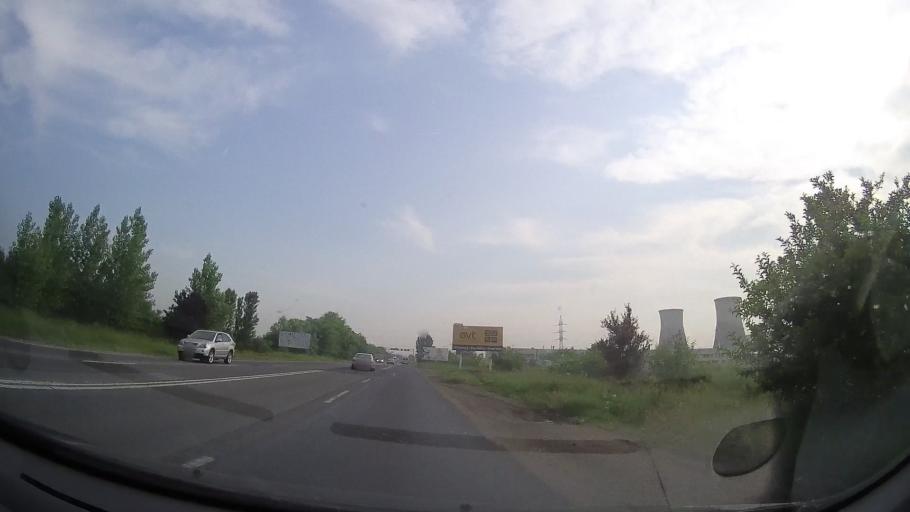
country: RO
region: Timis
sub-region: Comuna Giroc
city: Chisoda
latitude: 45.7078
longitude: 21.1882
